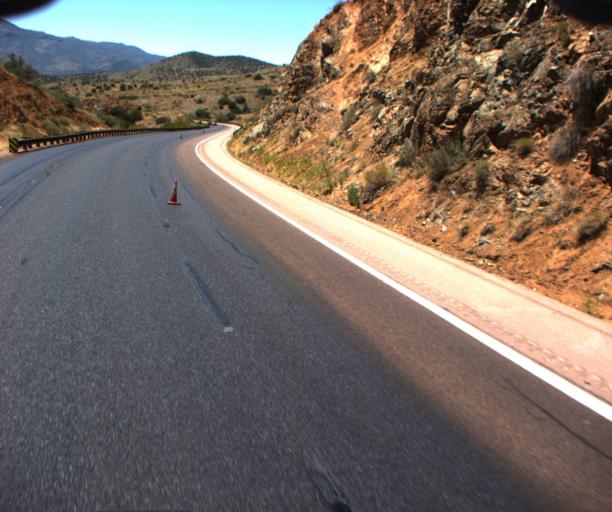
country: US
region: Arizona
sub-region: Gila County
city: Payson
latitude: 34.1530
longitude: -111.3426
